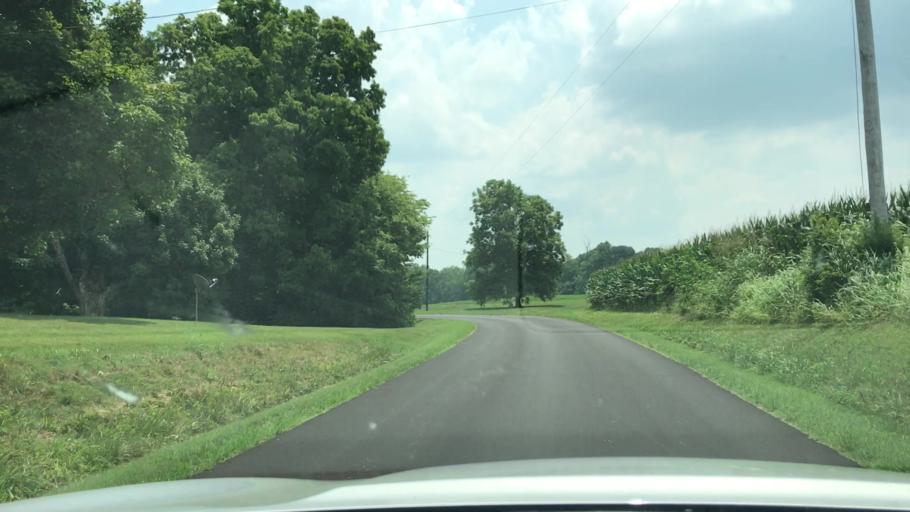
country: US
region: Kentucky
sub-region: Todd County
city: Elkton
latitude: 36.7749
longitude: -87.1440
